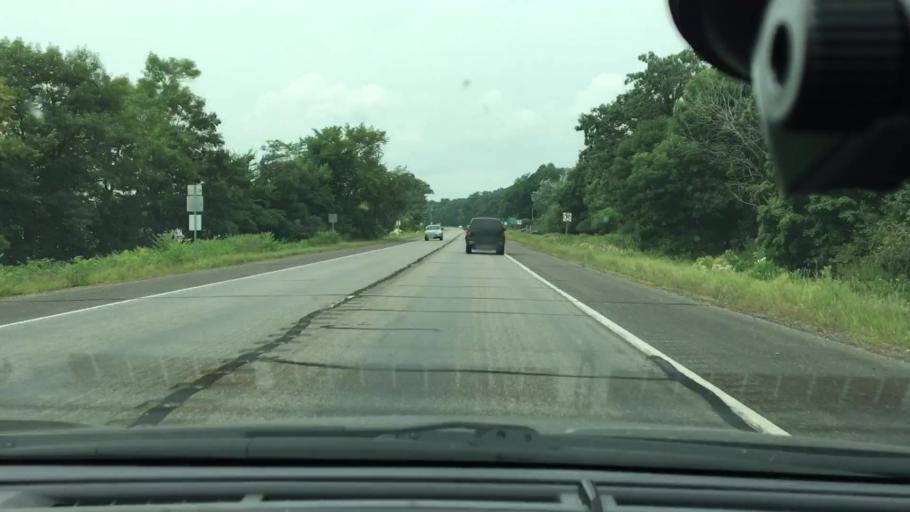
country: US
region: Minnesota
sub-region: Mille Lacs County
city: Vineland
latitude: 46.3270
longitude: -93.7808
